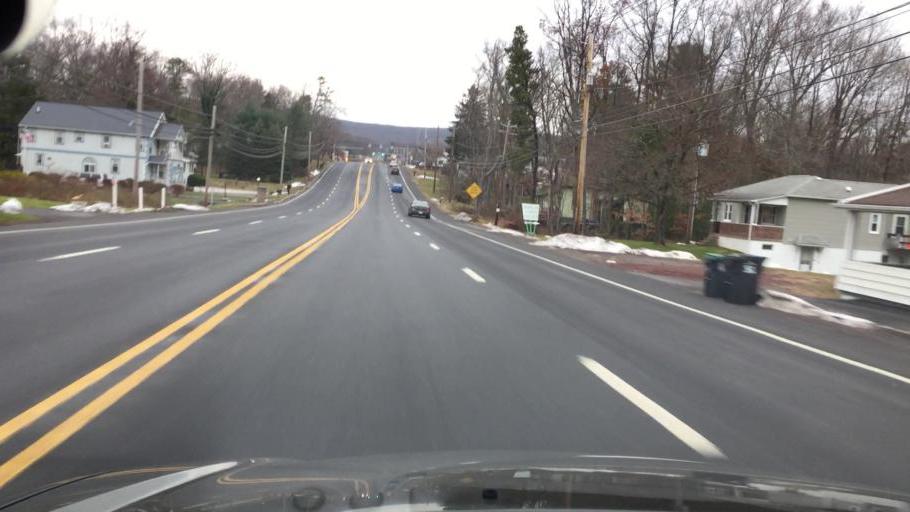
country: US
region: Pennsylvania
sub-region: Luzerne County
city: Oakdale
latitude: 41.0473
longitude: -75.9570
